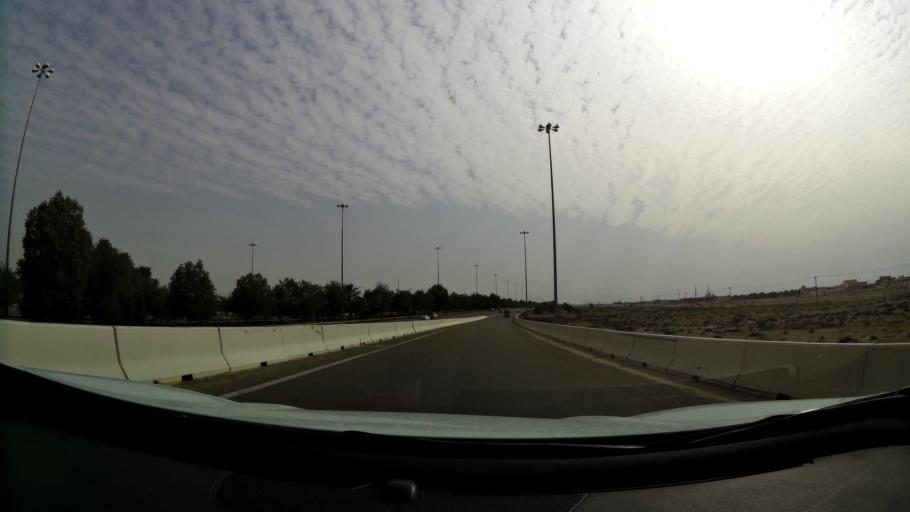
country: AE
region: Abu Dhabi
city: Abu Dhabi
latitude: 24.6202
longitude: 54.7161
